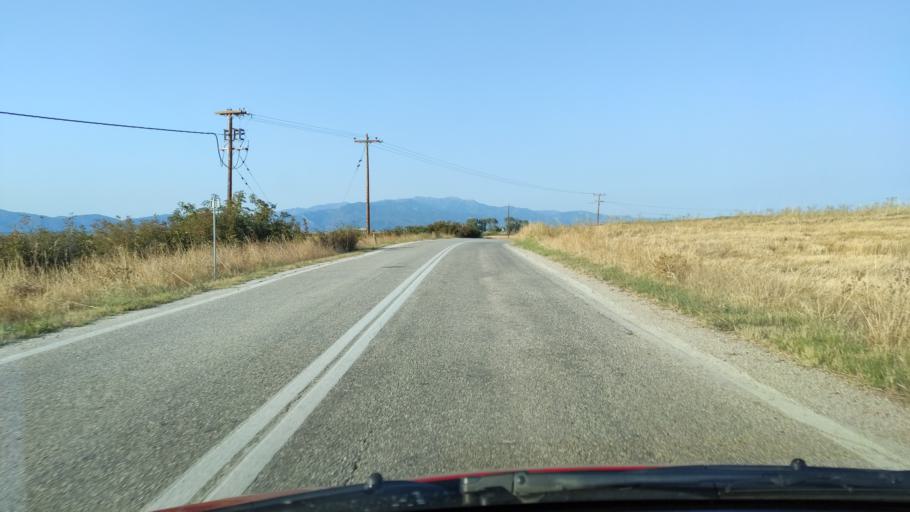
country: GR
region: East Macedonia and Thrace
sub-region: Nomos Rodopis
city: Iasmos
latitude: 40.9975
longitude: 25.1705
